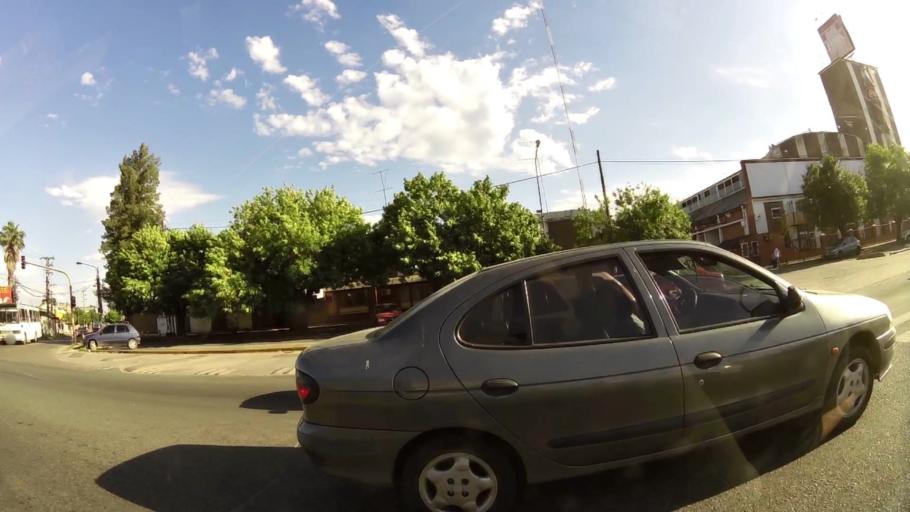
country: AR
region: Buenos Aires
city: Hurlingham
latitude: -34.5628
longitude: -58.6137
